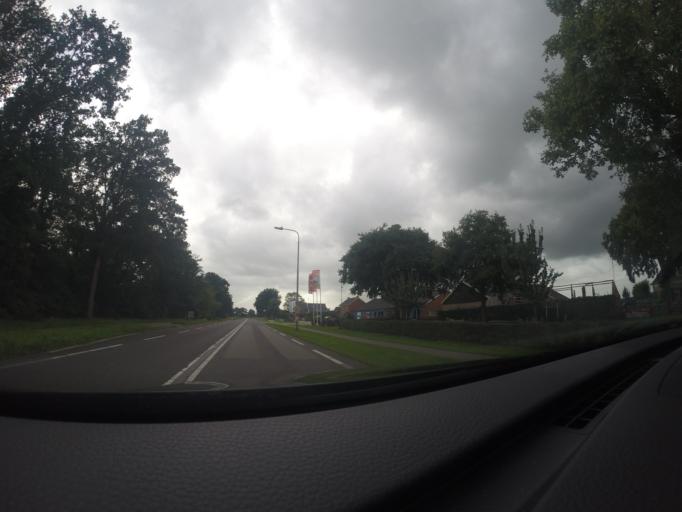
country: NL
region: Overijssel
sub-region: Gemeente Hof van Twente
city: Markelo
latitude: 52.2586
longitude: 6.5294
